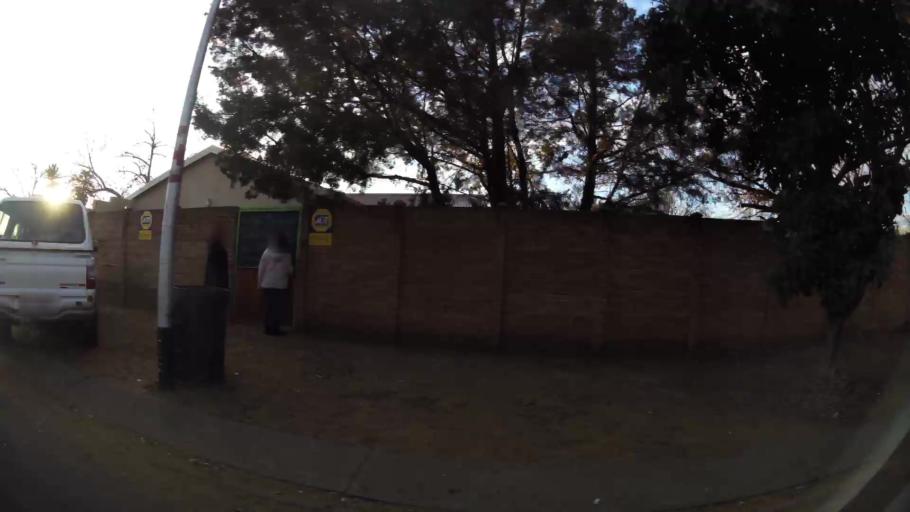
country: ZA
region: Orange Free State
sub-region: Mangaung Metropolitan Municipality
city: Bloemfontein
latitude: -29.1386
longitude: 26.1808
